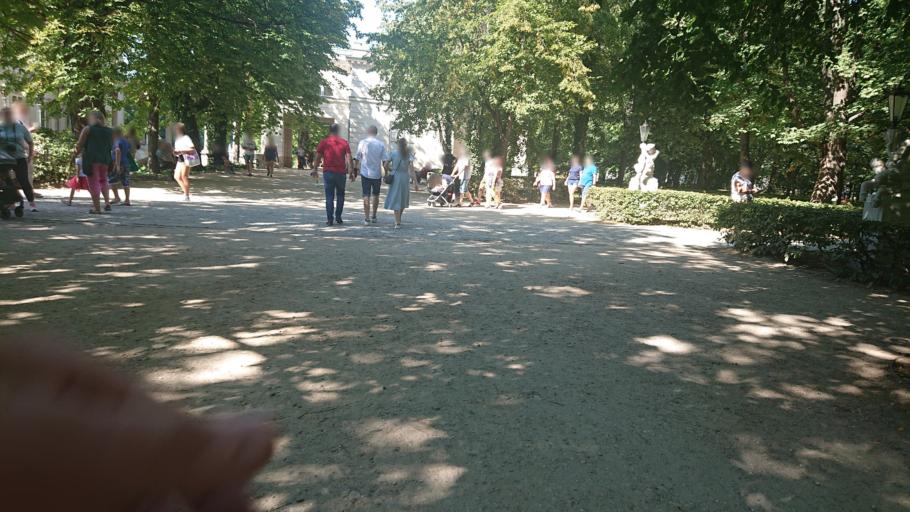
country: PL
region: Masovian Voivodeship
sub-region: Warszawa
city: Mokotow
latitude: 52.2147
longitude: 21.0365
